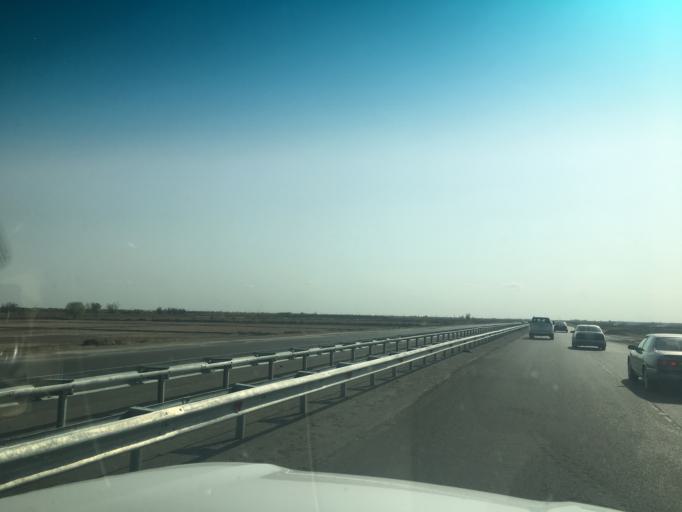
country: TM
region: Lebap
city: Farap
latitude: 39.1878
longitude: 63.5788
